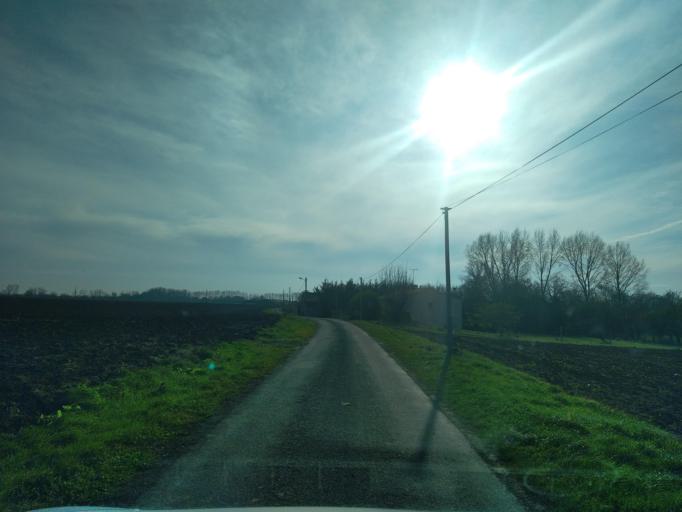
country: FR
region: Pays de la Loire
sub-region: Departement de la Vendee
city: Maillezais
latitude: 46.3535
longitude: -0.7359
